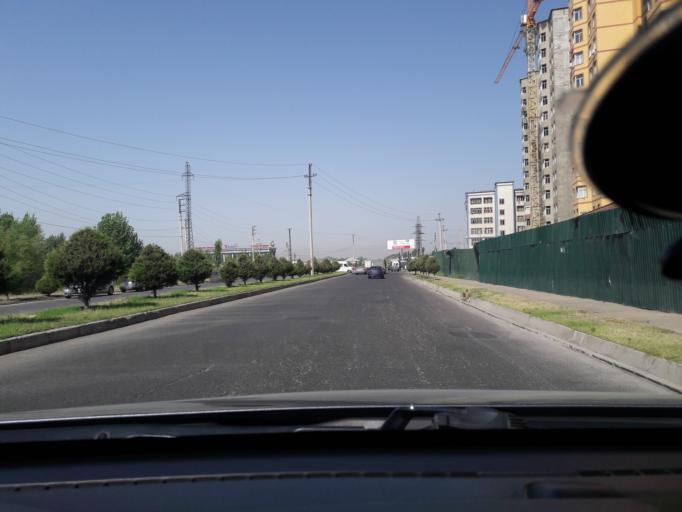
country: TJ
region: Dushanbe
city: Dushanbe
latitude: 38.5010
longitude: 68.7589
